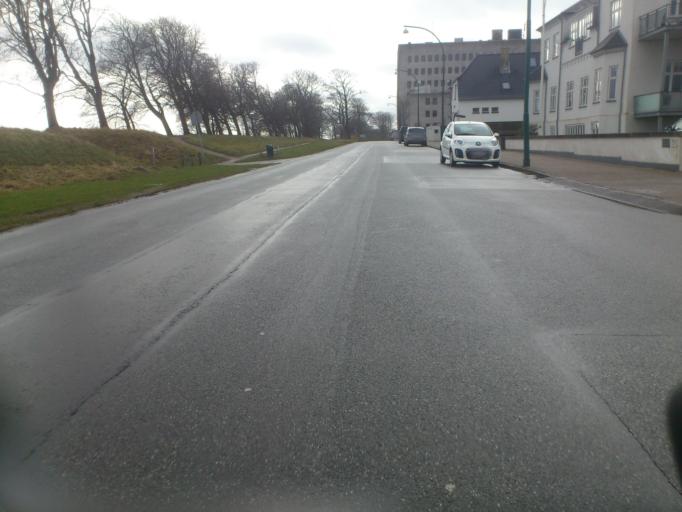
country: DK
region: South Denmark
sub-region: Fredericia Kommune
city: Fredericia
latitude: 55.5648
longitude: 9.7676
